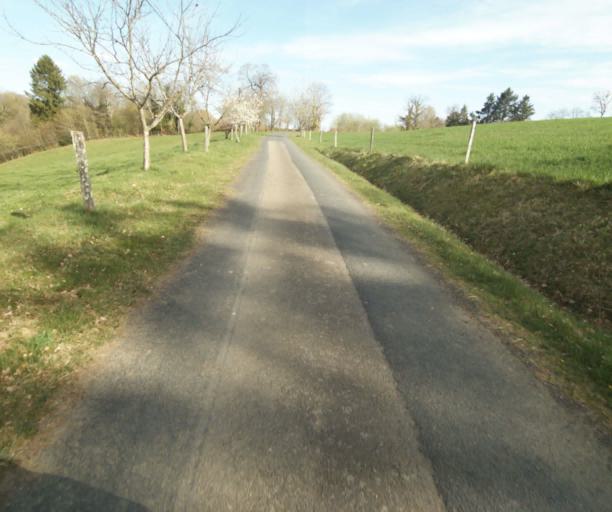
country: FR
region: Limousin
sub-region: Departement de la Correze
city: Naves
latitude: 45.3034
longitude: 1.7321
